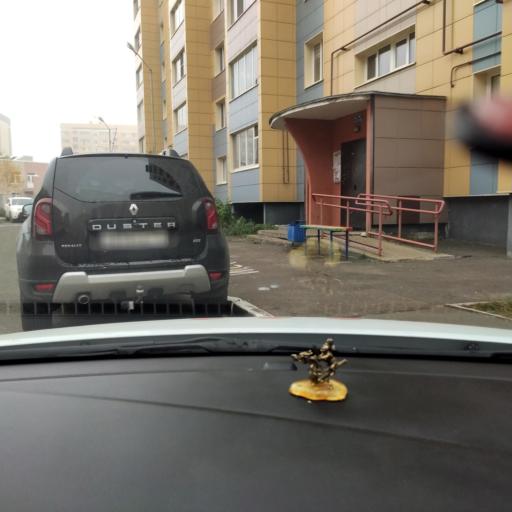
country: RU
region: Tatarstan
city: Osinovo
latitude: 55.8700
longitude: 48.8796
